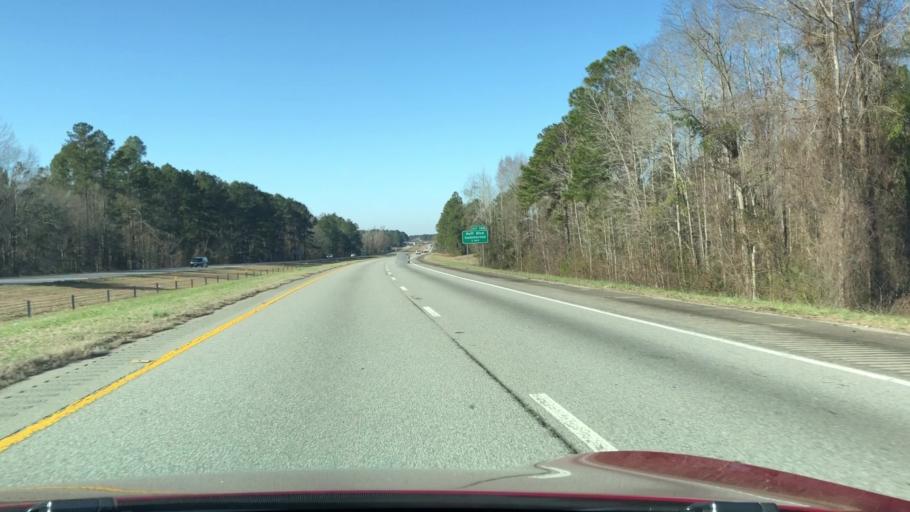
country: US
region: South Carolina
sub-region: Clarendon County
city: Manning
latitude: 33.5973
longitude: -80.3338
